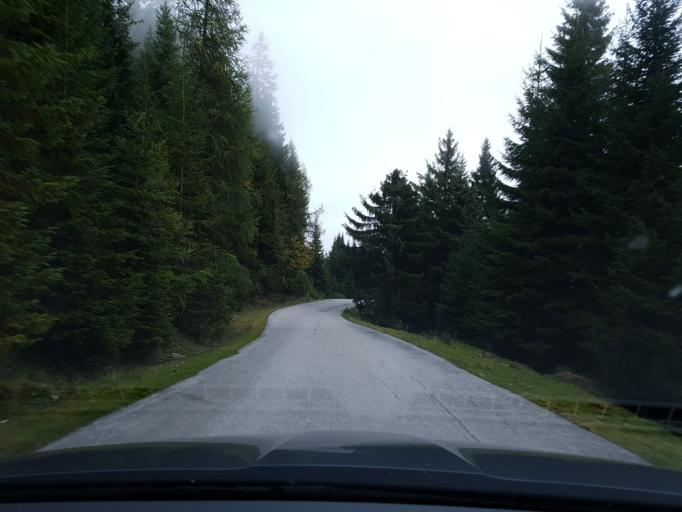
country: AT
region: Salzburg
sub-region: Politischer Bezirk Sankt Johann im Pongau
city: Filzmoos
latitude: 47.4087
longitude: 13.4968
